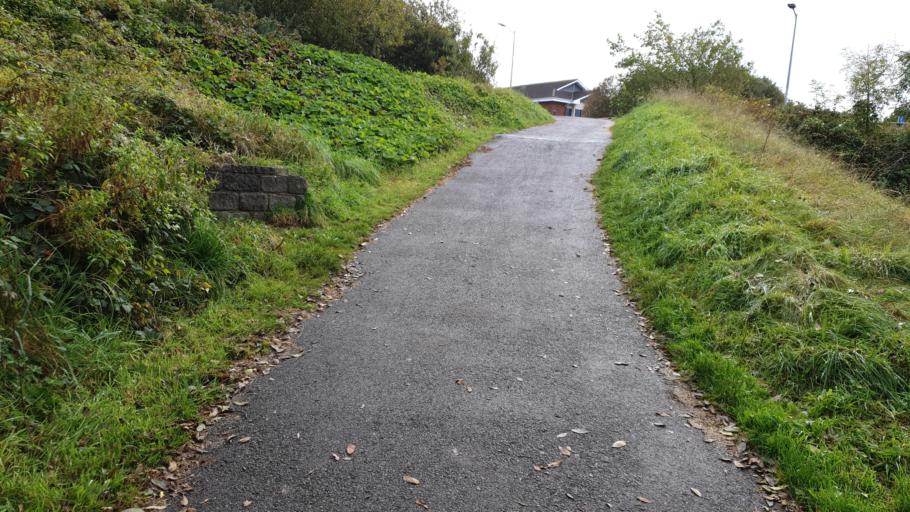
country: IE
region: Munster
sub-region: County Cork
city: Cork
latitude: 51.8908
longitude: -8.4122
